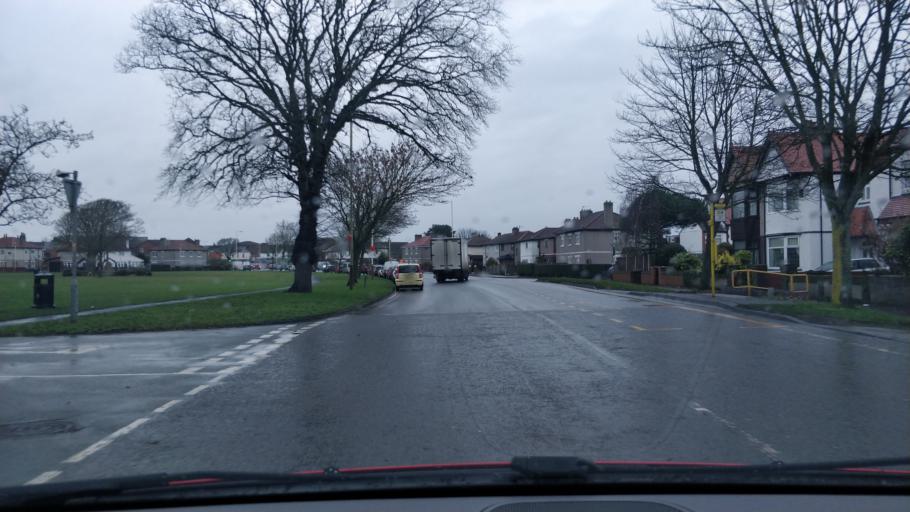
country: GB
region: England
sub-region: Sefton
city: Southport
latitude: 53.6004
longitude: -3.0334
